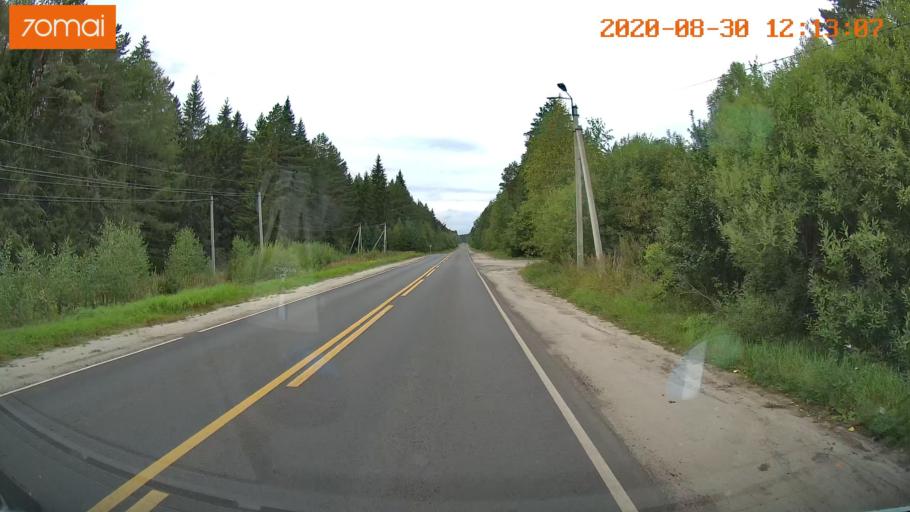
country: RU
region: Ivanovo
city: Yur'yevets
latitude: 57.3122
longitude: 43.0847
